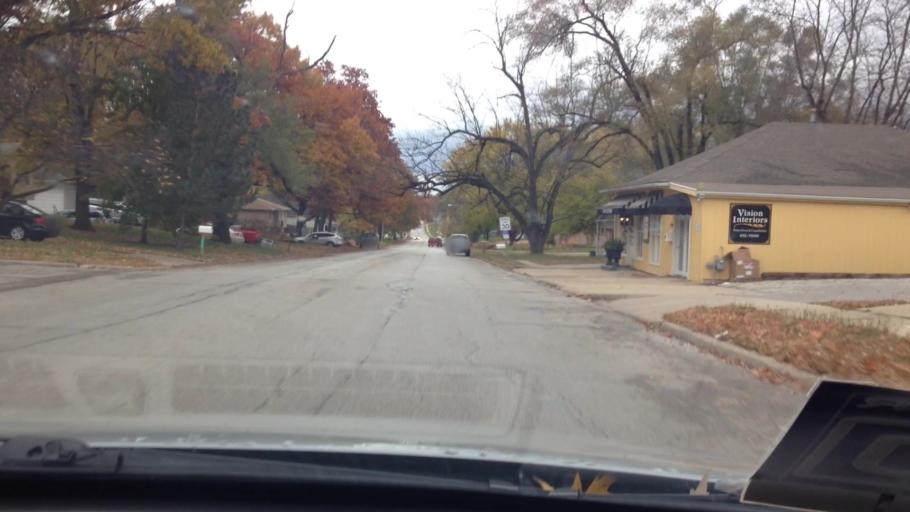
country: US
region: Kansas
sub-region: Leavenworth County
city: Leavenworth
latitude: 39.3007
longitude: -94.9137
